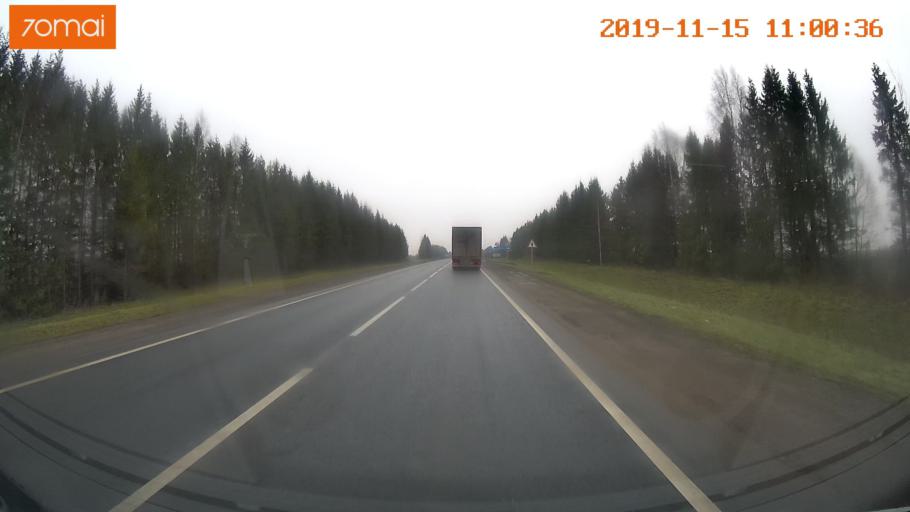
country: RU
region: Vologda
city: Chebsara
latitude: 59.1363
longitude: 38.9032
